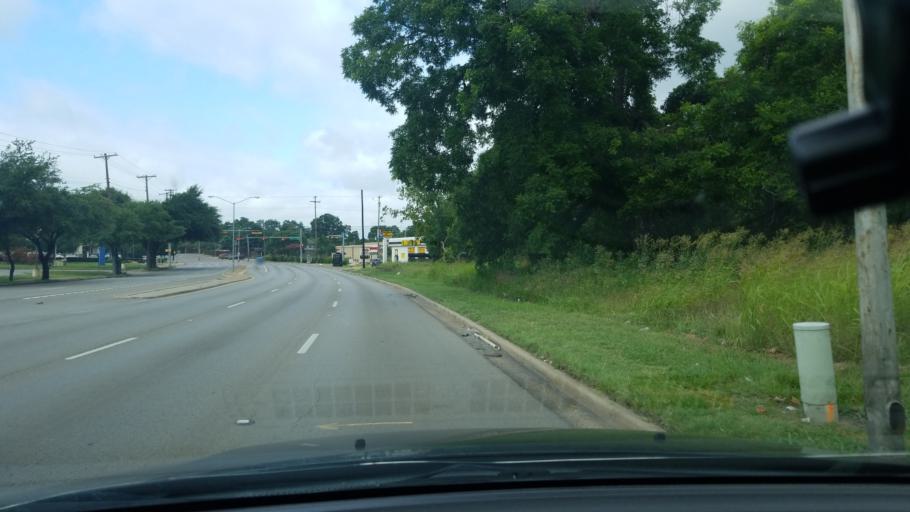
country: US
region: Texas
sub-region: Dallas County
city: Highland Park
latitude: 32.8126
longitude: -96.6999
